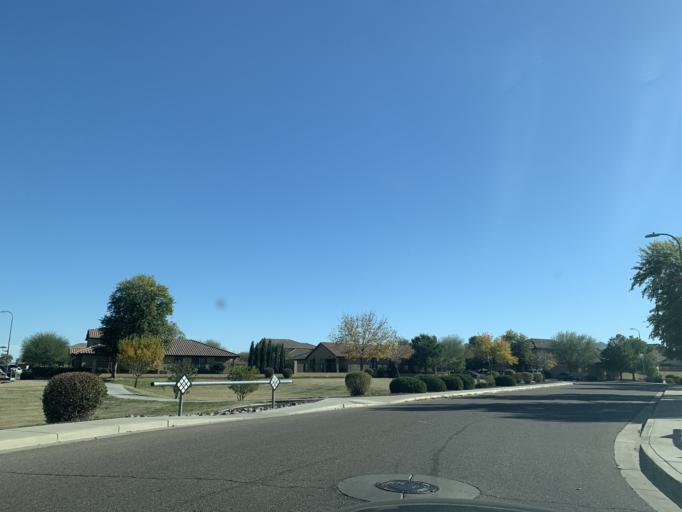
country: US
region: Arizona
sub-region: Maricopa County
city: Laveen
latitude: 33.3972
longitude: -112.1198
